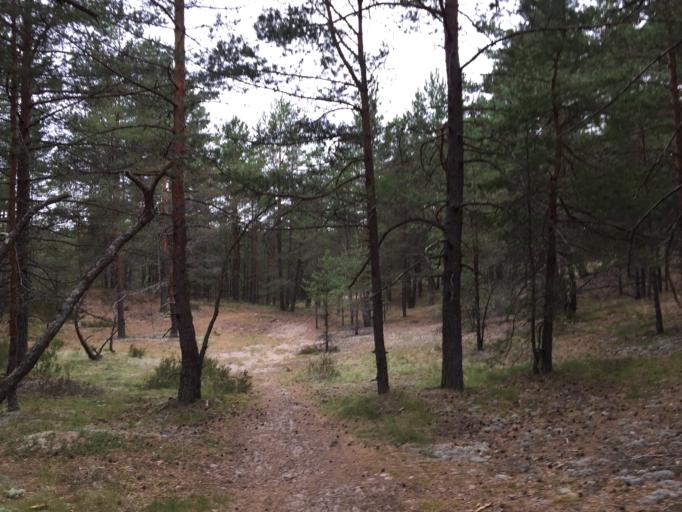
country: LV
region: Carnikava
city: Carnikava
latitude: 57.1219
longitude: 24.2176
